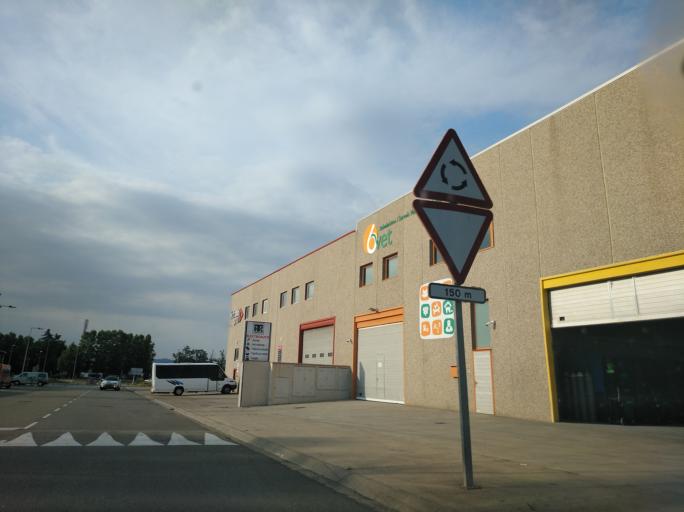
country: ES
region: Catalonia
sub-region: Provincia de Girona
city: Vilablareix
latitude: 41.9679
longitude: 2.7707
